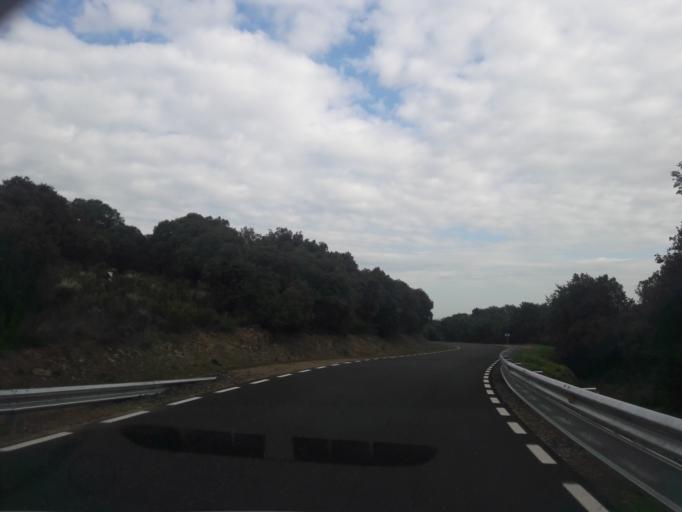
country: ES
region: Castille and Leon
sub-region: Provincia de Salamanca
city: Pastores
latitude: 40.5162
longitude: -6.5275
